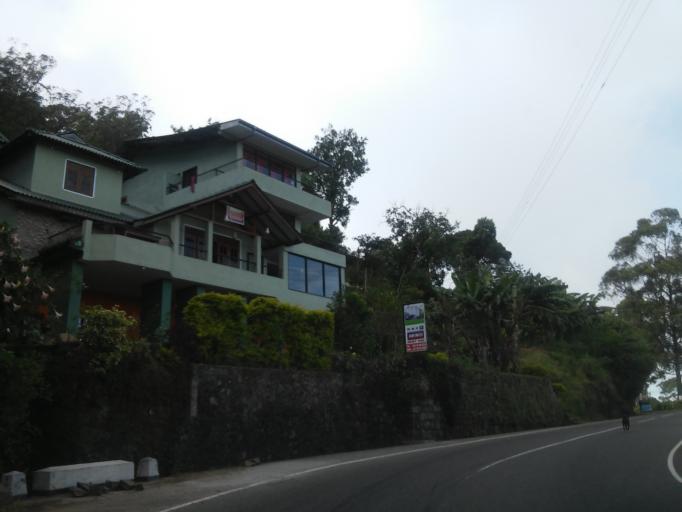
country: LK
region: Uva
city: Haputale
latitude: 6.7746
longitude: 80.9631
